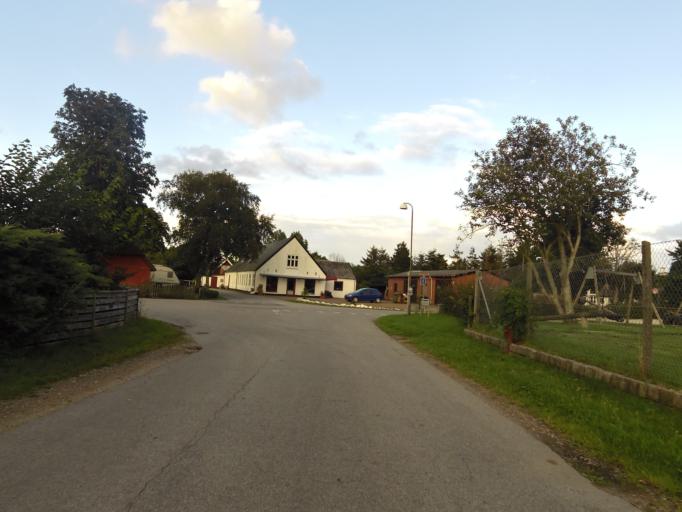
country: DK
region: South Denmark
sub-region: Esbjerg Kommune
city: Ribe
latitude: 55.3098
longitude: 8.7754
